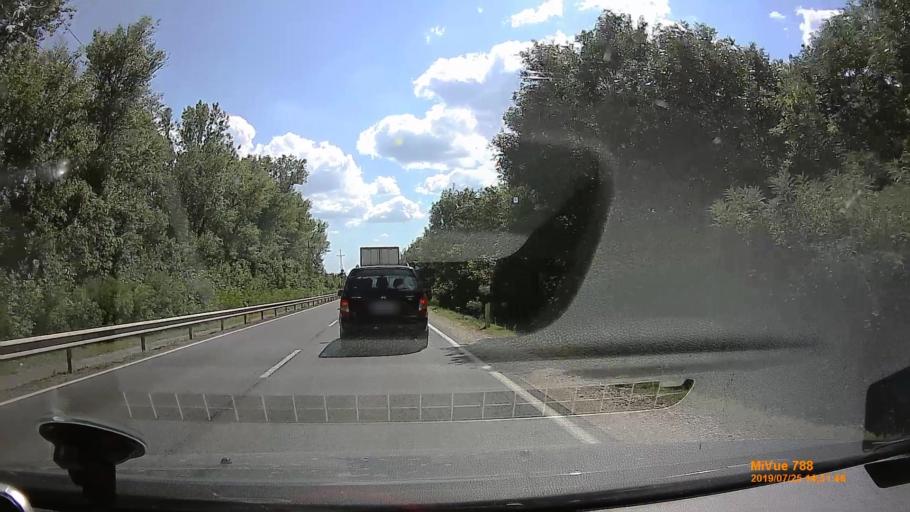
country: HU
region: Borsod-Abauj-Zemplen
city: Szikszo
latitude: 48.2110
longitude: 20.9395
